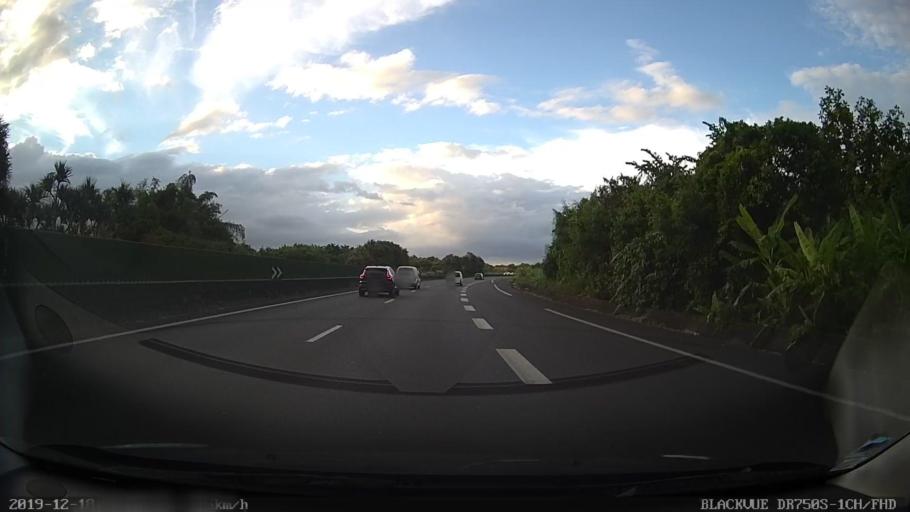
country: RE
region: Reunion
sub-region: Reunion
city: Saint-Andre
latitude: -20.9829
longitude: 55.6554
